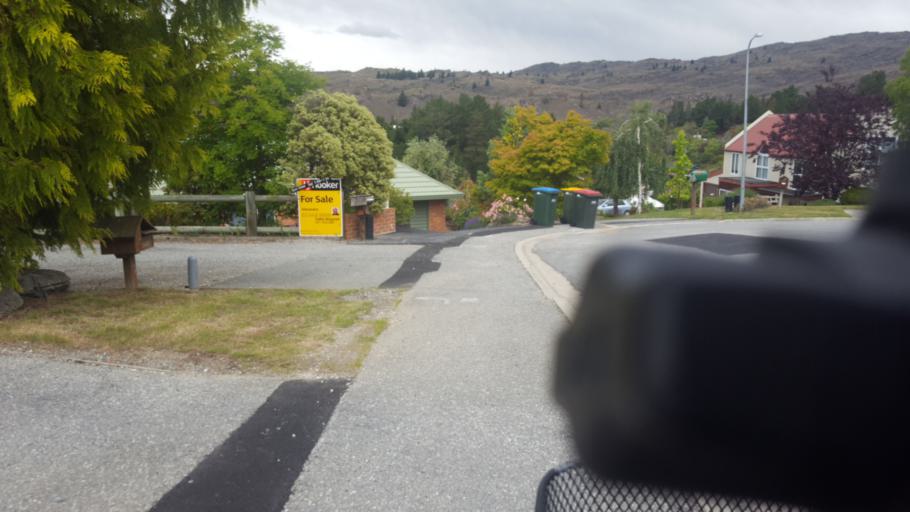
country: NZ
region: Otago
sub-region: Queenstown-Lakes District
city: Wanaka
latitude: -45.2613
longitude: 169.3823
